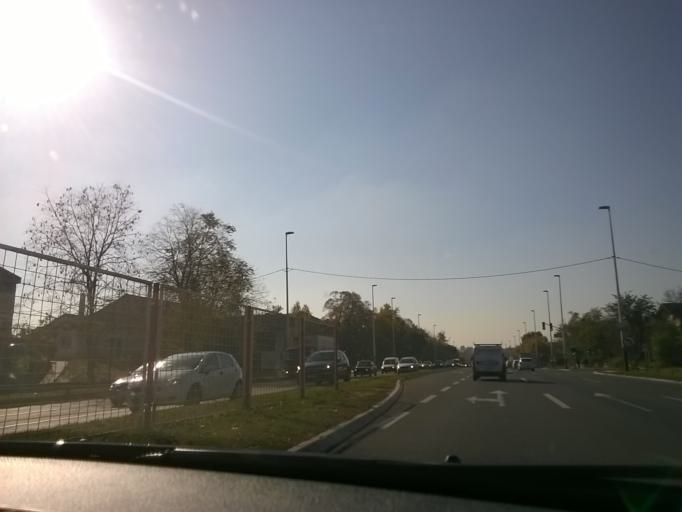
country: RS
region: Central Serbia
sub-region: Belgrade
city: Zemun
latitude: 44.8426
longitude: 20.3684
